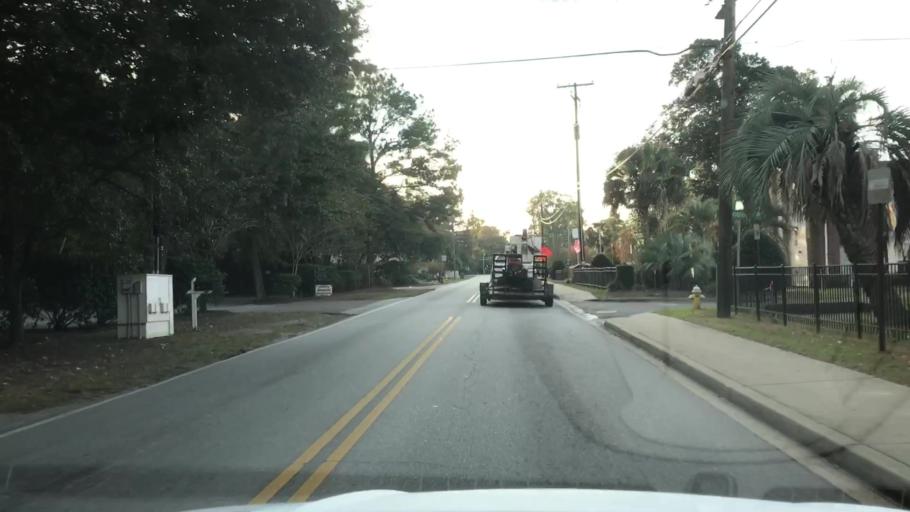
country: US
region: South Carolina
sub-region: Charleston County
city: North Charleston
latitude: 32.8122
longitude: -80.0123
